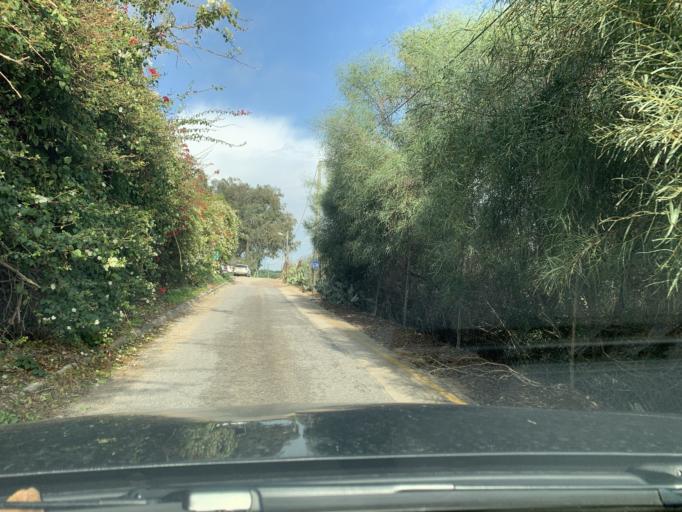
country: PS
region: West Bank
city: Qalqilyah
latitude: 32.1957
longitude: 34.9530
